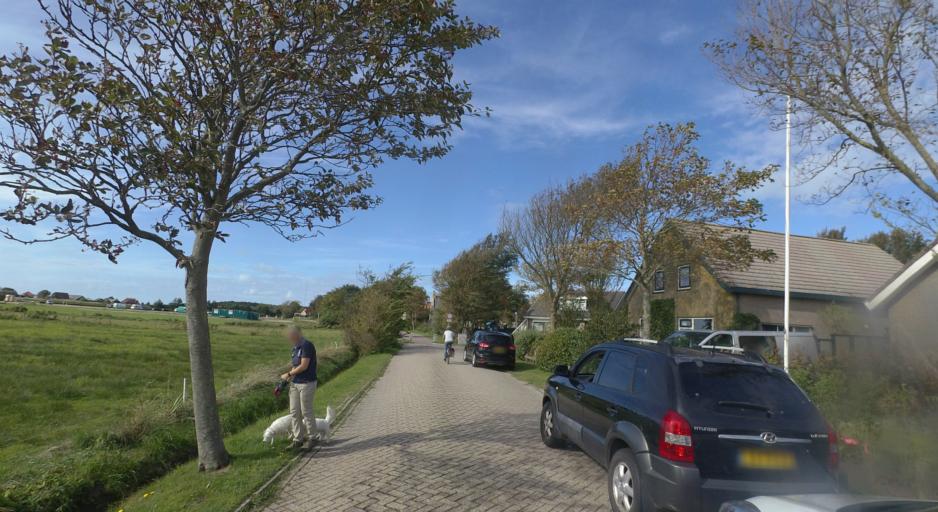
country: NL
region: Friesland
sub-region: Gemeente Ameland
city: Nes
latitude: 53.4428
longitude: 5.7720
